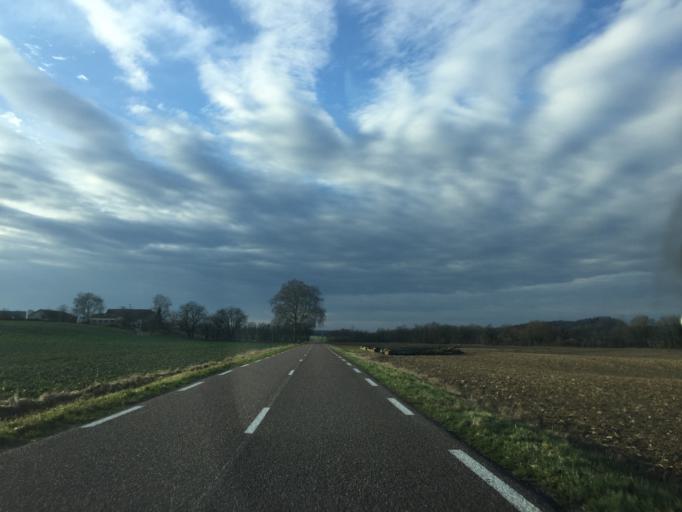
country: FR
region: Franche-Comte
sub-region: Departement du Jura
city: Arbois
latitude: 46.9194
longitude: 5.7240
